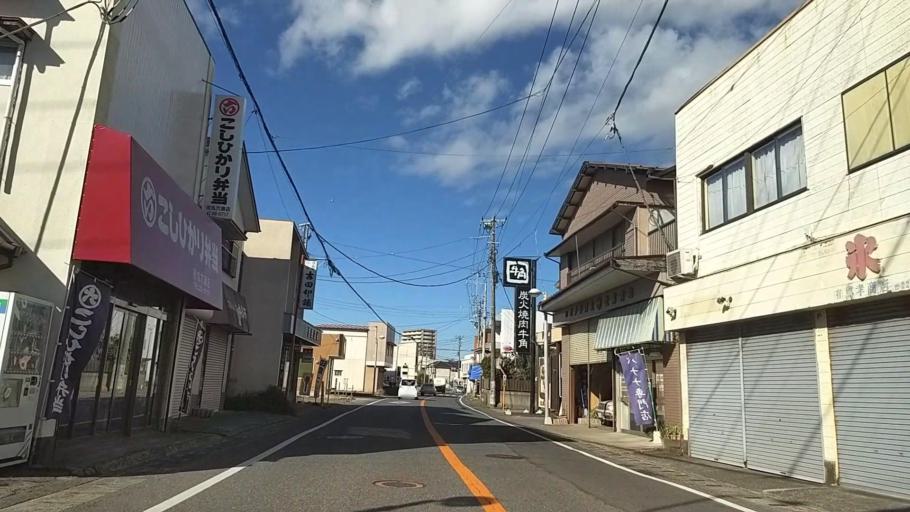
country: JP
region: Chiba
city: Tateyama
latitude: 34.9920
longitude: 139.8676
